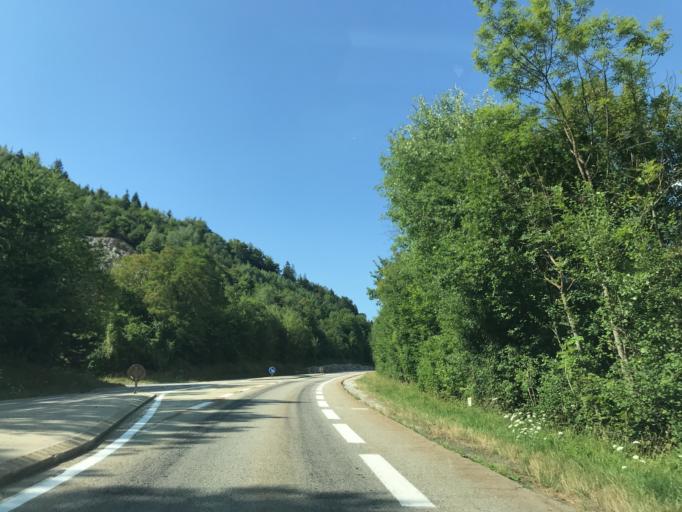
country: FR
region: Rhone-Alpes
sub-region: Departement de la Haute-Savoie
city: Dingy-Saint-Clair
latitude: 45.9108
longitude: 6.1981
